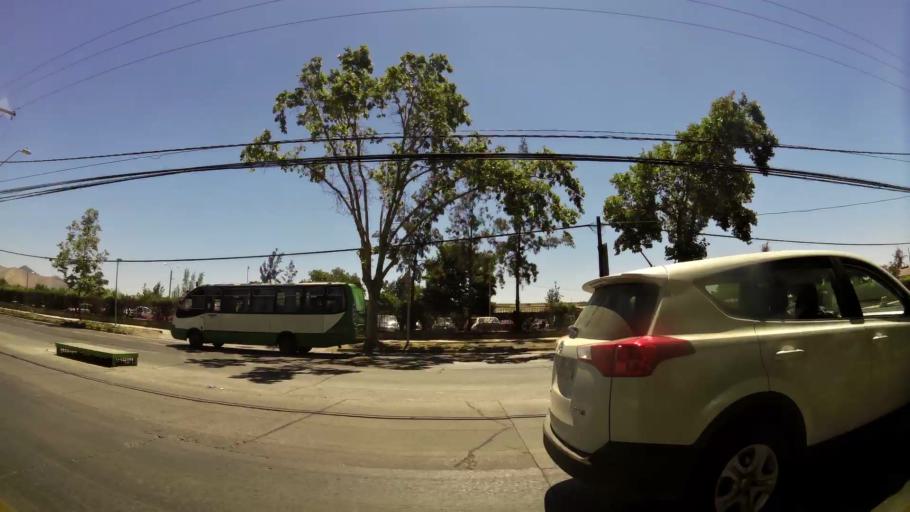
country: CL
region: Santiago Metropolitan
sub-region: Provincia de Maipo
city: San Bernardo
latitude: -33.5704
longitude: -70.6877
